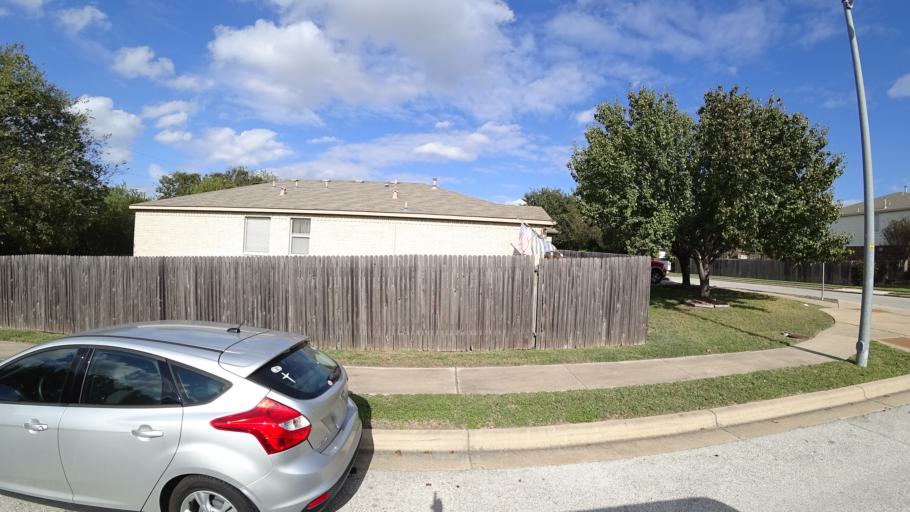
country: US
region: Texas
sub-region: Travis County
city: Pflugerville
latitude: 30.4304
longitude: -97.6406
